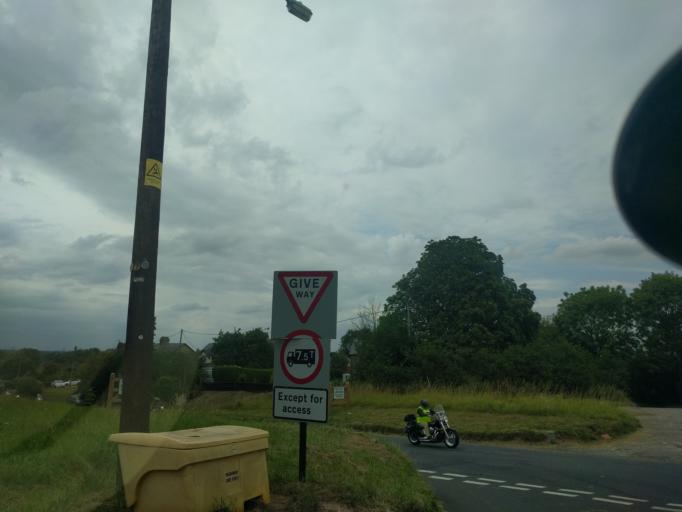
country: GB
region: England
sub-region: Wiltshire
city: Lacock
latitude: 51.4112
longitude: -2.1042
